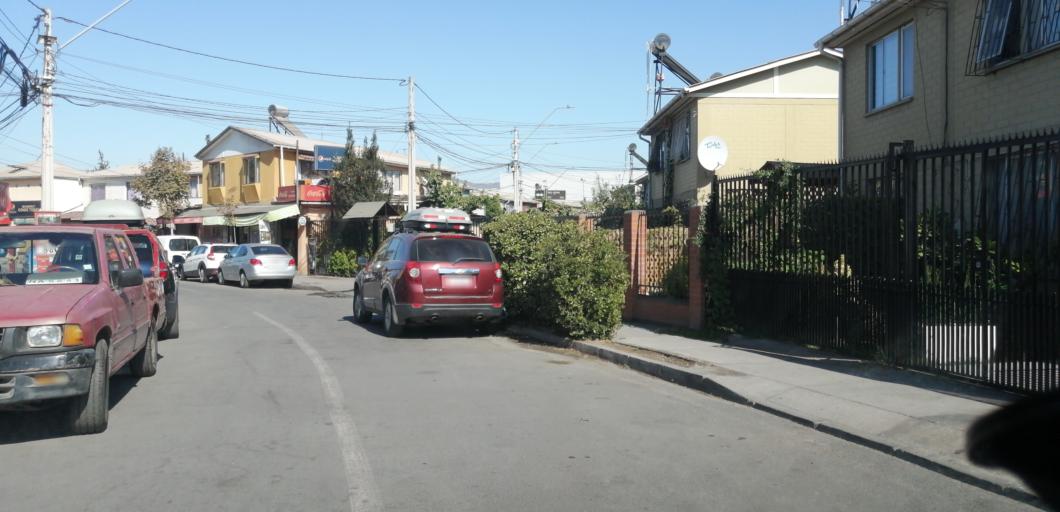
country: CL
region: Santiago Metropolitan
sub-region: Provincia de Santiago
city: Lo Prado
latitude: -33.4448
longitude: -70.7695
